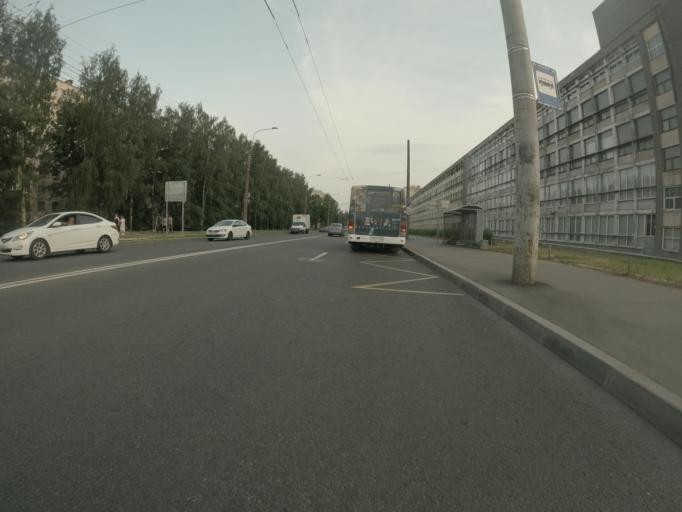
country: RU
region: Leningrad
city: Kalininskiy
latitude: 59.9866
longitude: 30.4015
